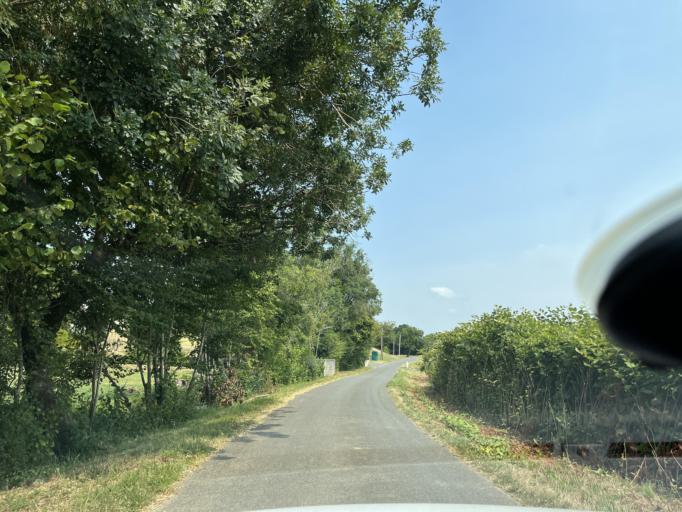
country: FR
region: Poitou-Charentes
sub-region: Departement de la Charente-Maritime
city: Pons
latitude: 45.5895
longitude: -0.5757
